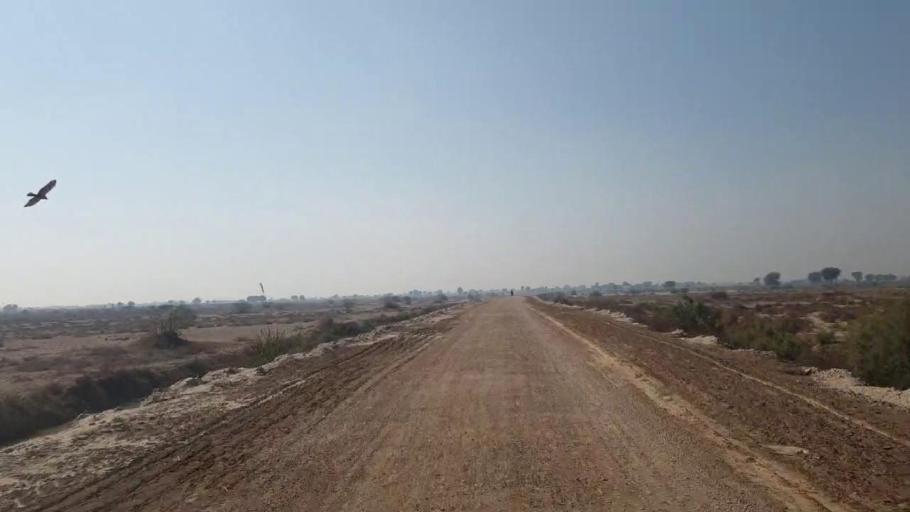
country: PK
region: Sindh
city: Shahpur Chakar
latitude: 26.1151
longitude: 68.6107
